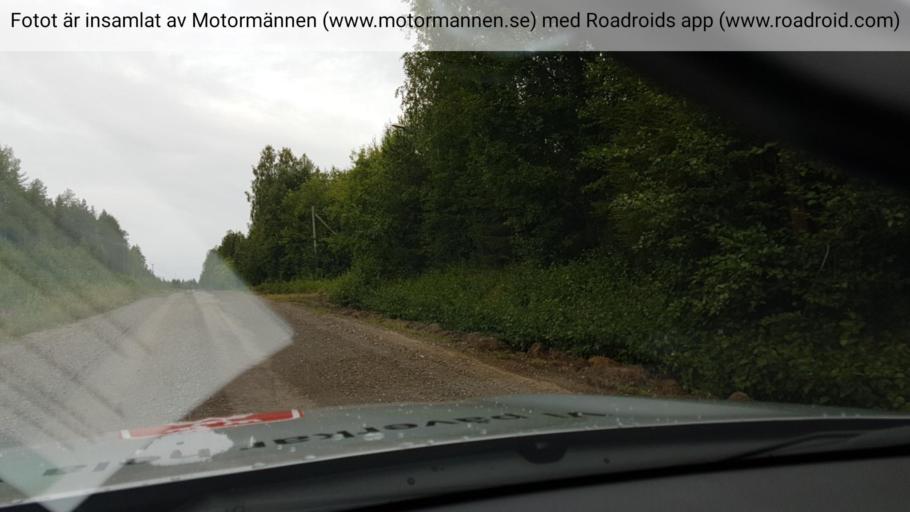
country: SE
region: Norrbotten
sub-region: Alvsbyns Kommun
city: AElvsbyn
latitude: 65.9970
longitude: 21.1742
